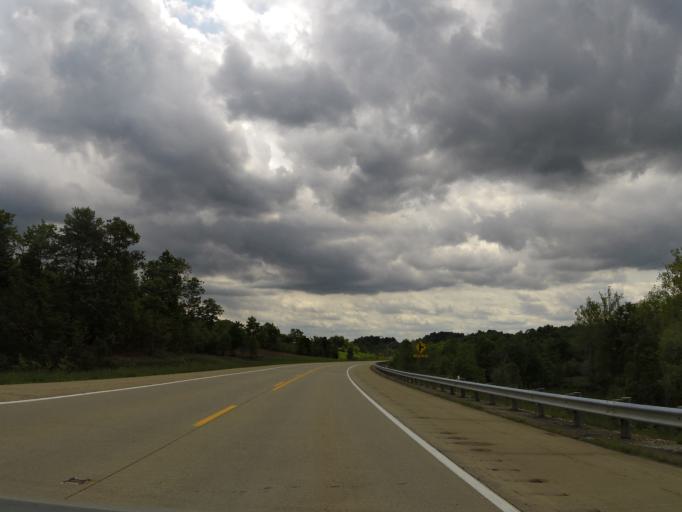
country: US
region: West Virginia
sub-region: Mason County
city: New Haven
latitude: 38.9883
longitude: -81.8667
